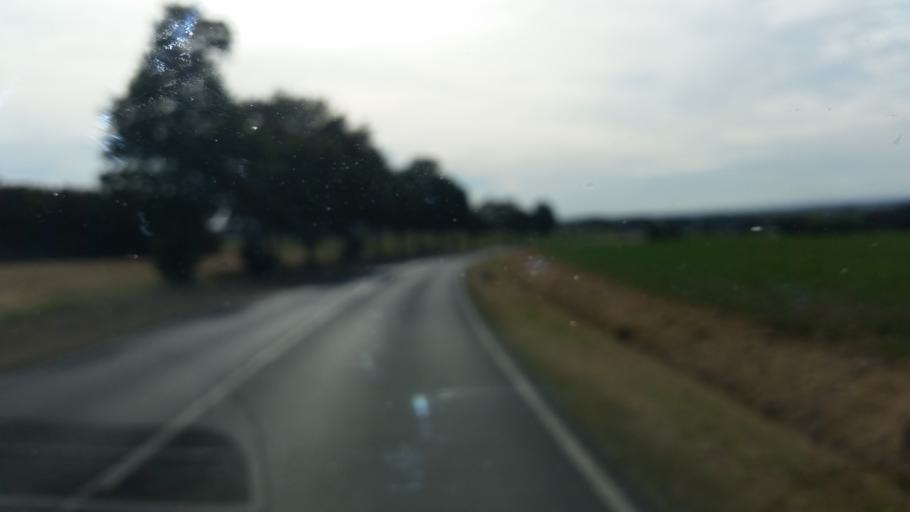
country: DE
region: Rheinland-Pfalz
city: Hahn
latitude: 49.9633
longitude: 7.2853
